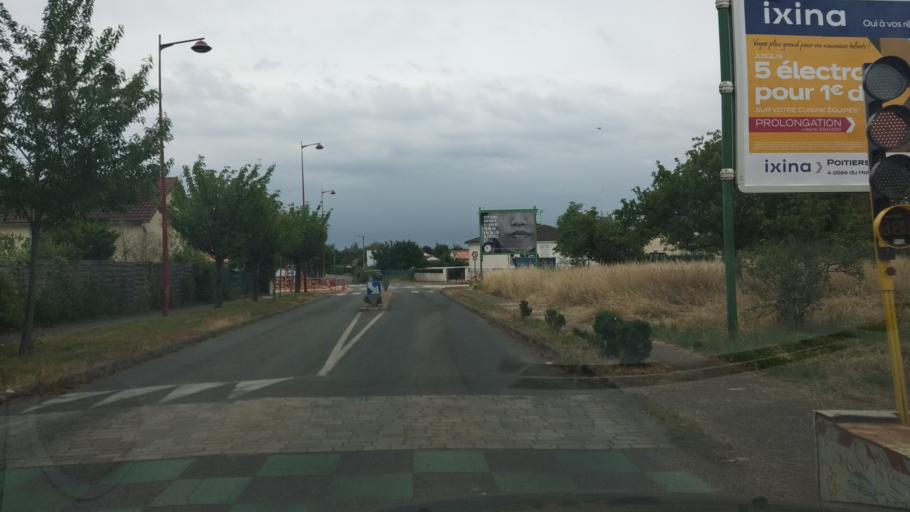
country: FR
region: Poitou-Charentes
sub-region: Departement de la Vienne
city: Biard
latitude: 46.5763
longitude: 0.3091
